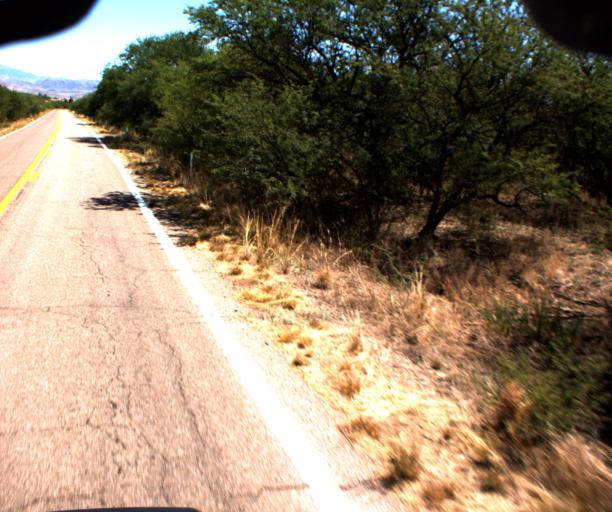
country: US
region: Arizona
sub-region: Santa Cruz County
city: Rio Rico
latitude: 31.4242
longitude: -111.0103
